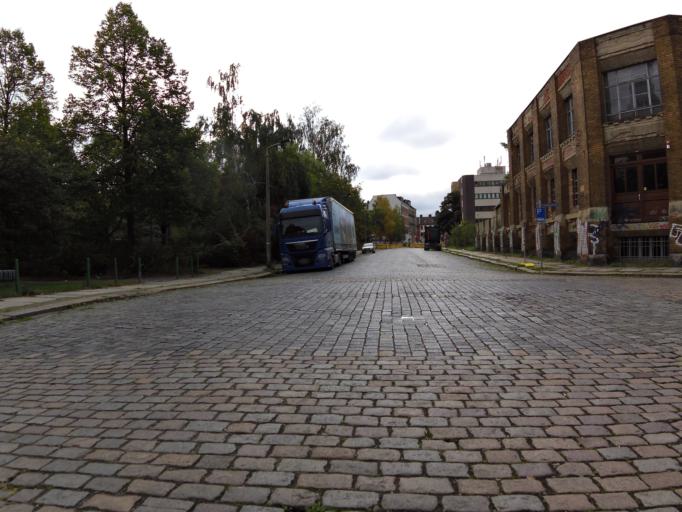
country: DE
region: Saxony
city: Leipzig
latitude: 51.3377
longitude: 12.3979
